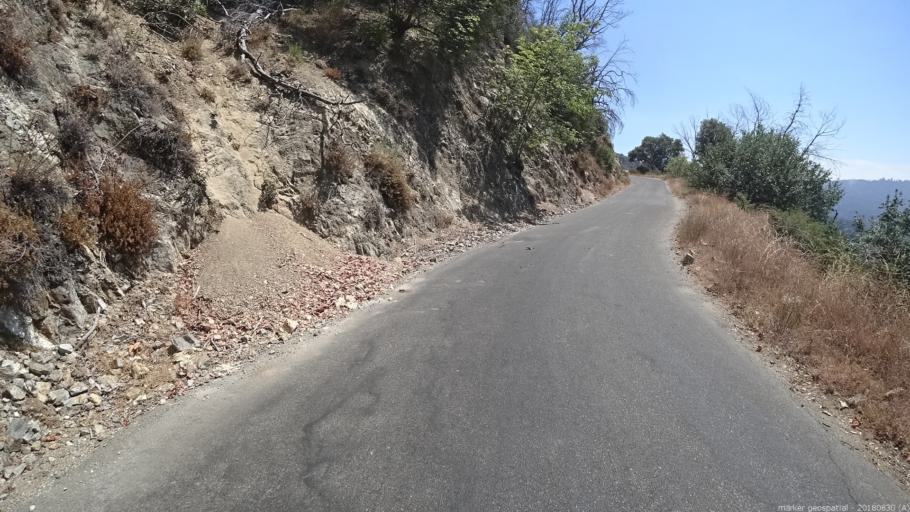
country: US
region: California
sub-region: Monterey County
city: Greenfield
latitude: 36.0106
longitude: -121.4581
